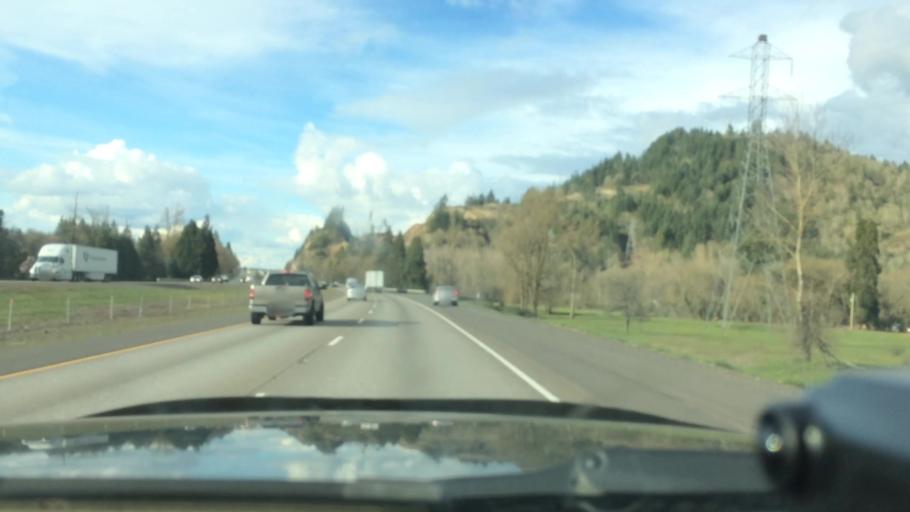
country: US
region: Oregon
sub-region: Lane County
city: Coburg
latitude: 44.1054
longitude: -123.0440
